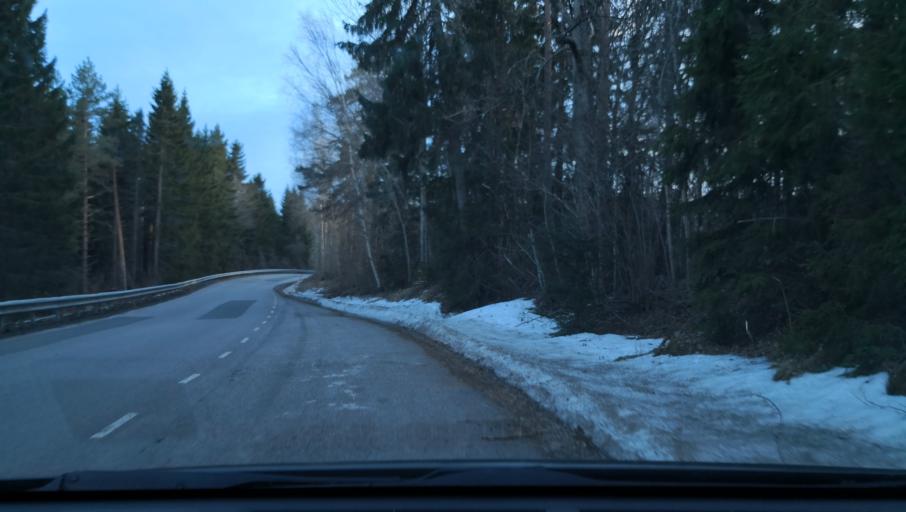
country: SE
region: Uppsala
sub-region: Osthammars Kommun
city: Osterbybruk
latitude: 60.2262
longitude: 17.9187
